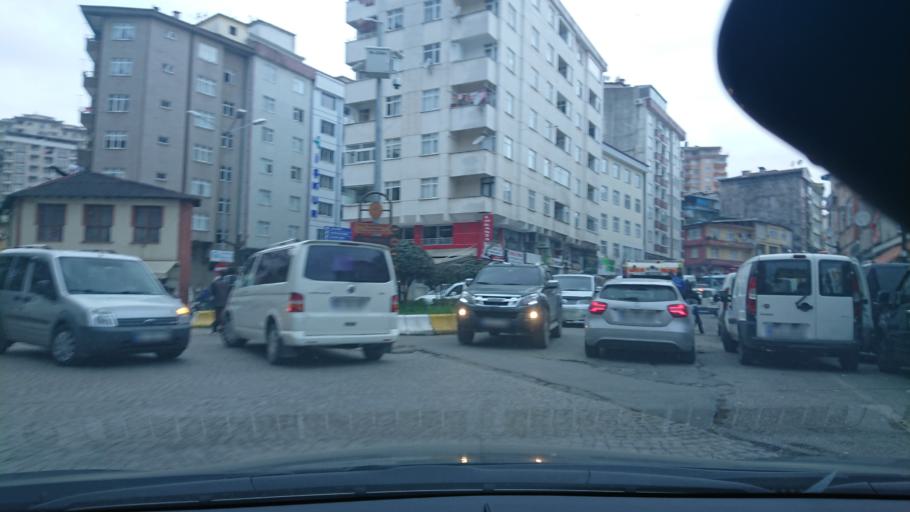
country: TR
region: Rize
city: Rize
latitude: 41.0265
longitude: 40.5149
